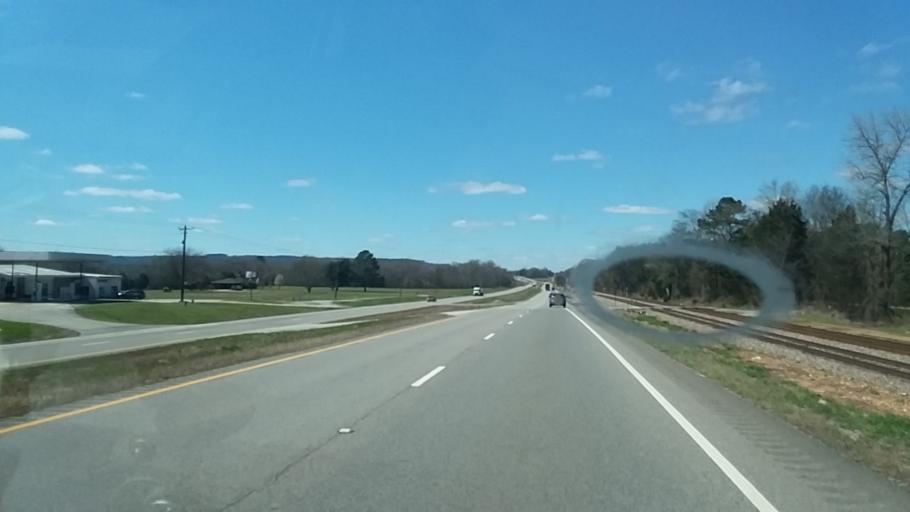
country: US
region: Alabama
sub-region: Colbert County
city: Tuscumbia
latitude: 34.7276
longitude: -87.8370
